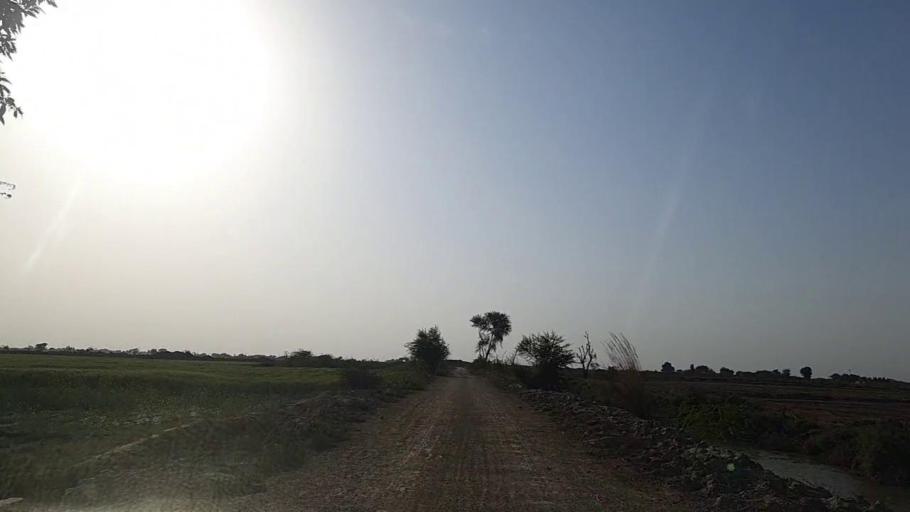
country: PK
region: Sindh
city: Dhoro Naro
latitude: 25.4255
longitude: 69.4806
